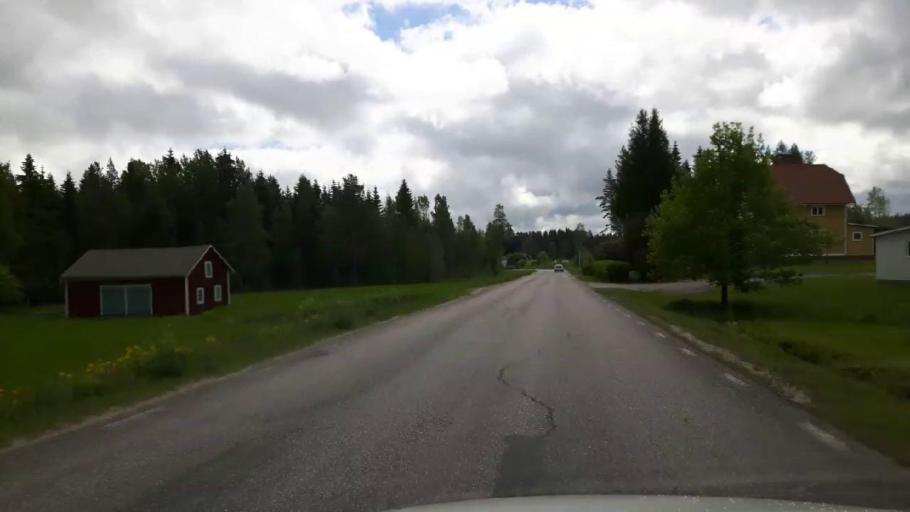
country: SE
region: Gaevleborg
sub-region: Ovanakers Kommun
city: Edsbyn
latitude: 61.3426
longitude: 15.9365
